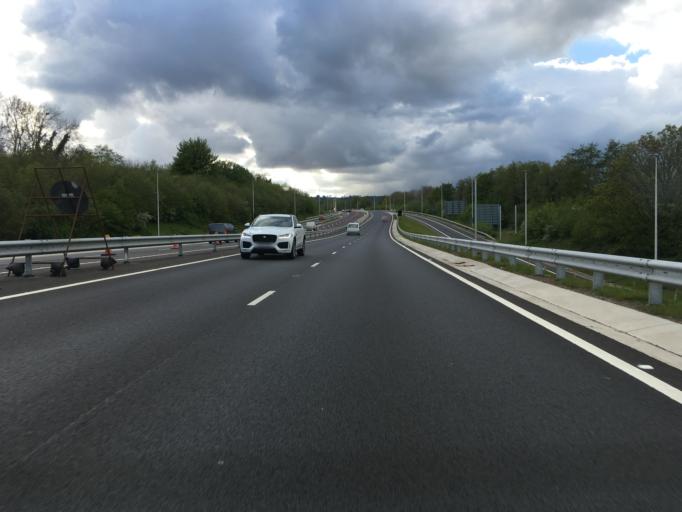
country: GB
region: Wales
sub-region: Monmouthshire
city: Gilwern
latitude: 51.8231
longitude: -3.0774
